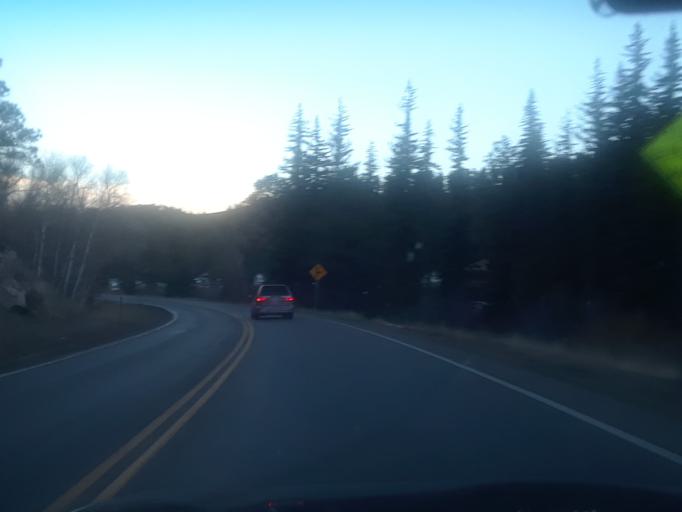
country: US
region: Colorado
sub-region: Jefferson County
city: Evergreen
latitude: 39.4175
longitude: -105.5264
